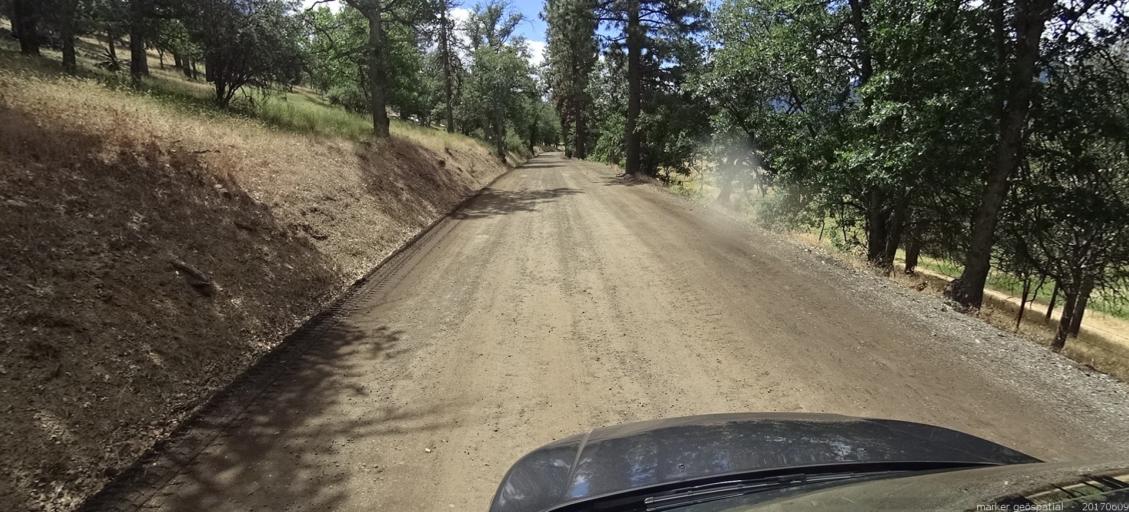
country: US
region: California
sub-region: Siskiyou County
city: Yreka
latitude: 41.4014
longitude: -122.8640
